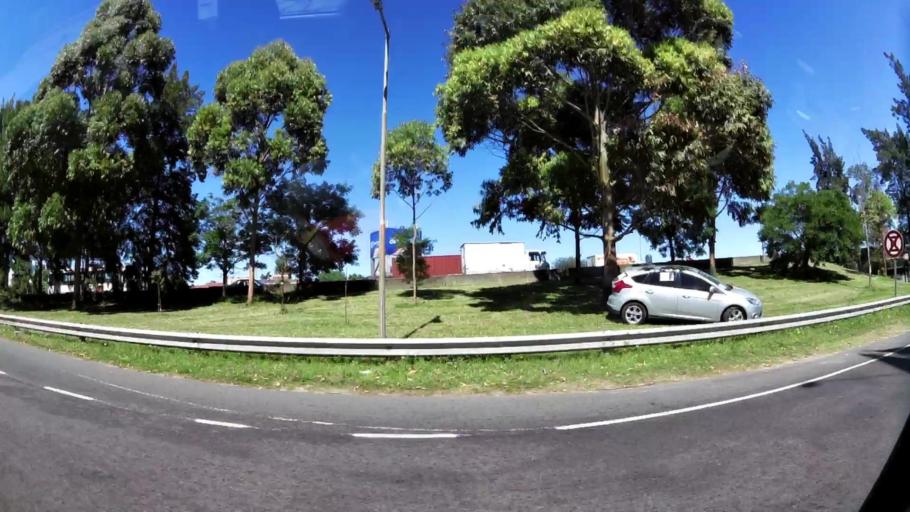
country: AR
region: Buenos Aires
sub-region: Partido de Vicente Lopez
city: Olivos
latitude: -34.5286
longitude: -58.5064
